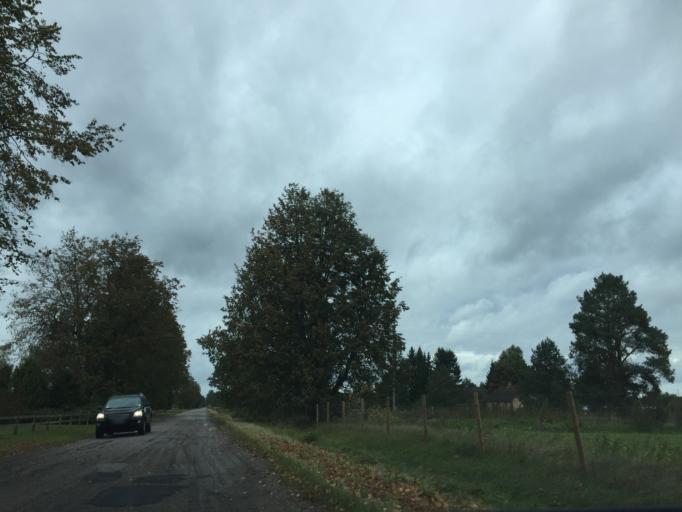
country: LV
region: Olaine
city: Olaine
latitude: 56.7666
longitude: 23.8815
